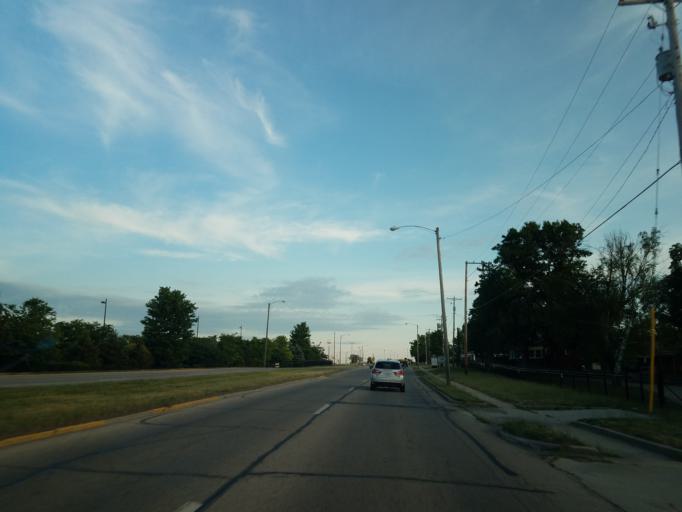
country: US
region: Illinois
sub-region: McLean County
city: Bloomington
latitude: 40.4548
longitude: -88.9927
